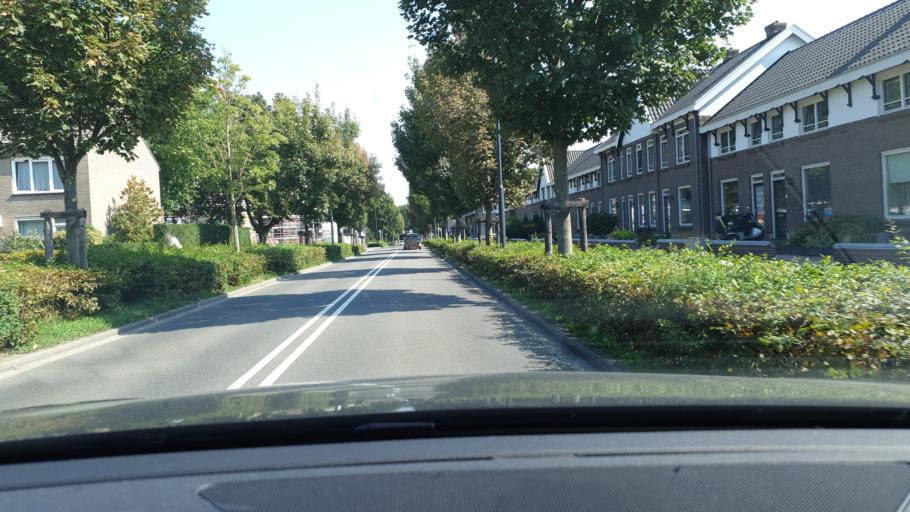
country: NL
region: Limburg
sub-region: Gemeente Sittard-Geleen
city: Sittard
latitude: 51.0059
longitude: 5.8558
